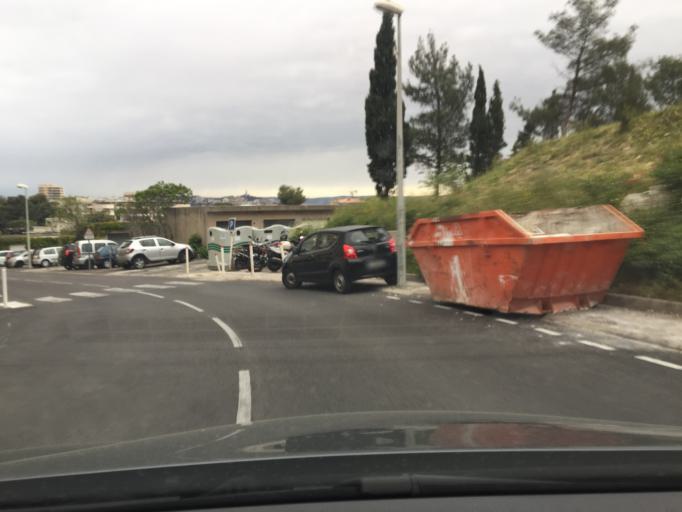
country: FR
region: Provence-Alpes-Cote d'Azur
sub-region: Departement des Bouches-du-Rhone
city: Marseille 09
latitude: 43.2540
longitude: 5.4258
